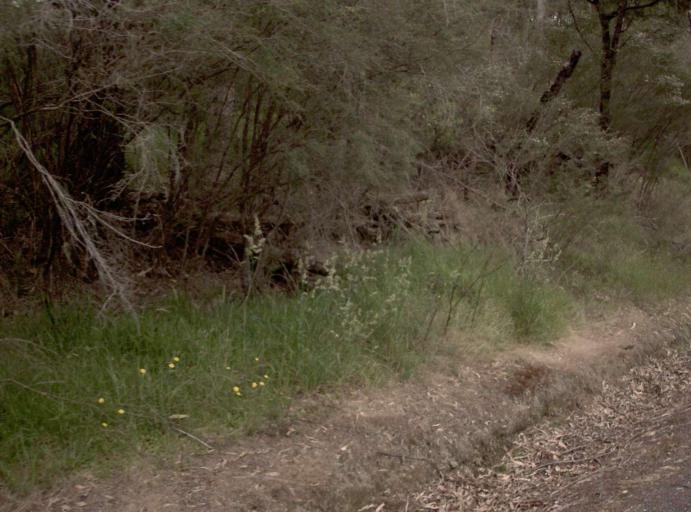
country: AU
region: New South Wales
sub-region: Bombala
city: Bombala
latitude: -37.3967
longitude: 149.1960
